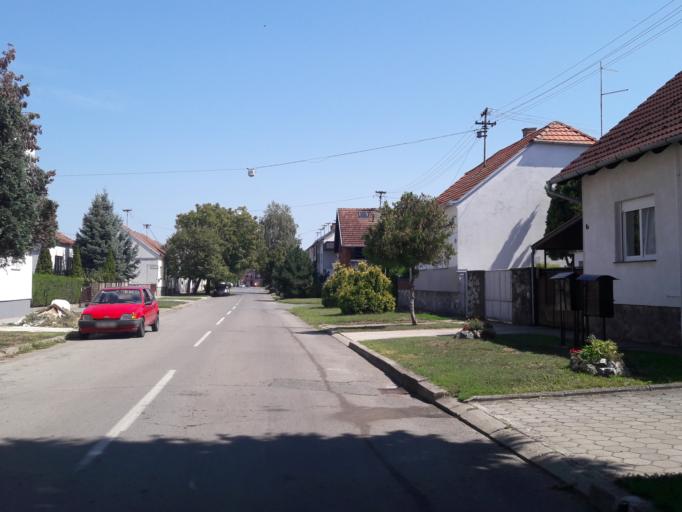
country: HR
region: Osjecko-Baranjska
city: Visnjevac
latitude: 45.5637
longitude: 18.6451
